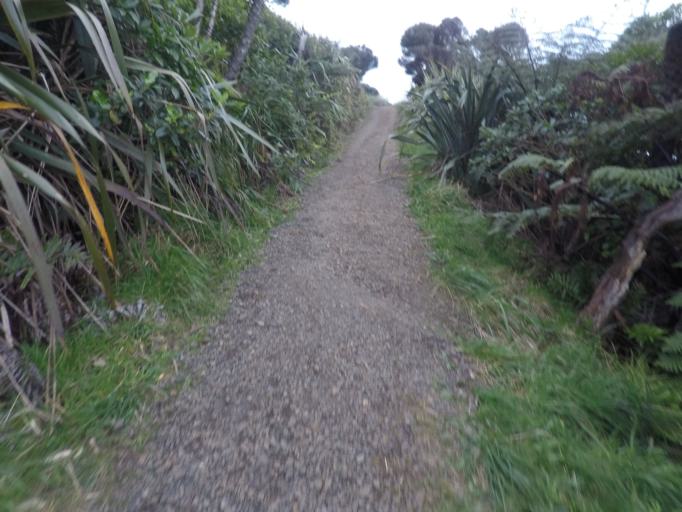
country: NZ
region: Auckland
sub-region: Auckland
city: Muriwai Beach
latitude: -36.9730
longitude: 174.4680
